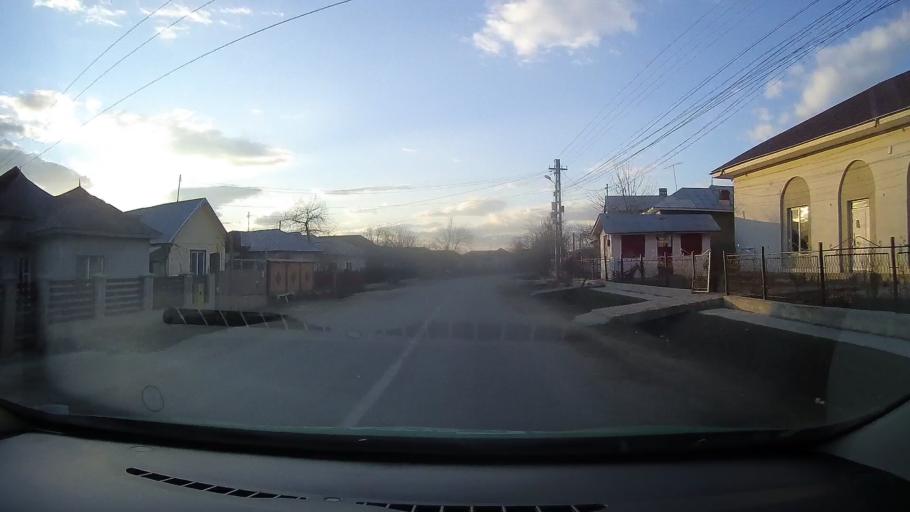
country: RO
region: Dambovita
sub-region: Comuna Gura Ocnitei
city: Adanca
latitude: 44.9207
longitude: 25.6139
